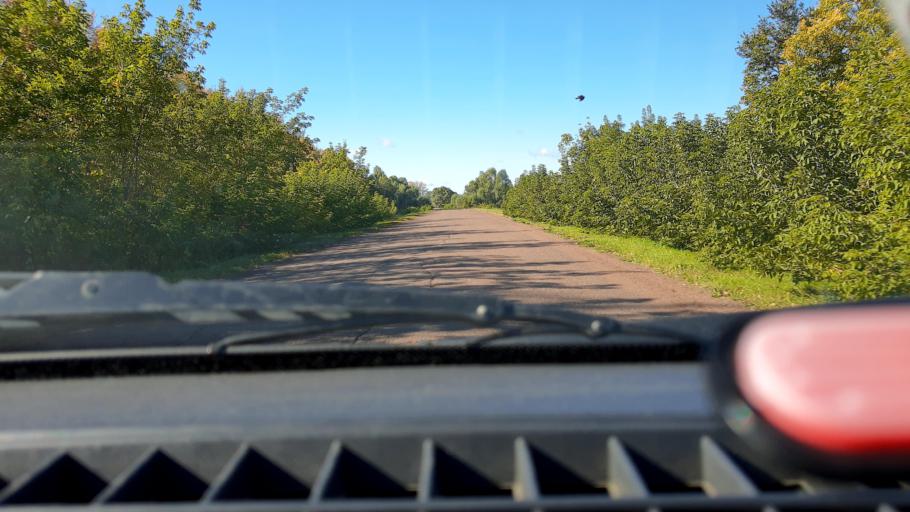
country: RU
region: Bashkortostan
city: Kushnarenkovo
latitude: 55.1088
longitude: 55.5268
